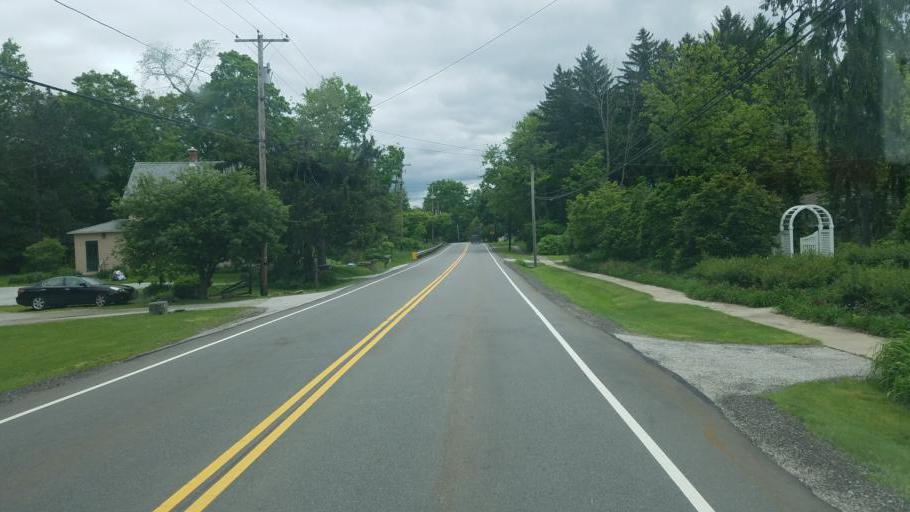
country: US
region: Ohio
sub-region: Summit County
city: Peninsula
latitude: 41.2419
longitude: -81.5598
